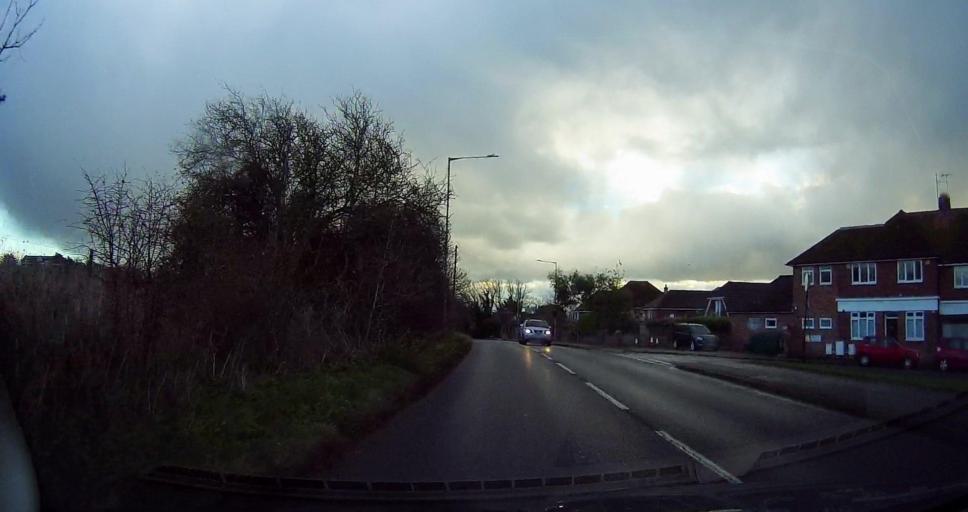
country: GB
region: England
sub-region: Brighton and Hove
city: Rottingdean
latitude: 50.8123
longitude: -0.0618
